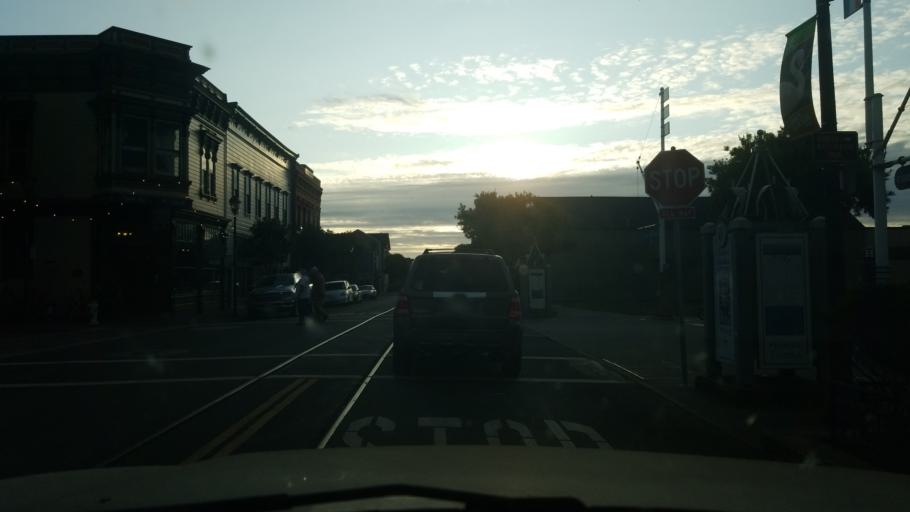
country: US
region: California
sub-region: Humboldt County
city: Eureka
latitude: 40.8053
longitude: -124.1665
